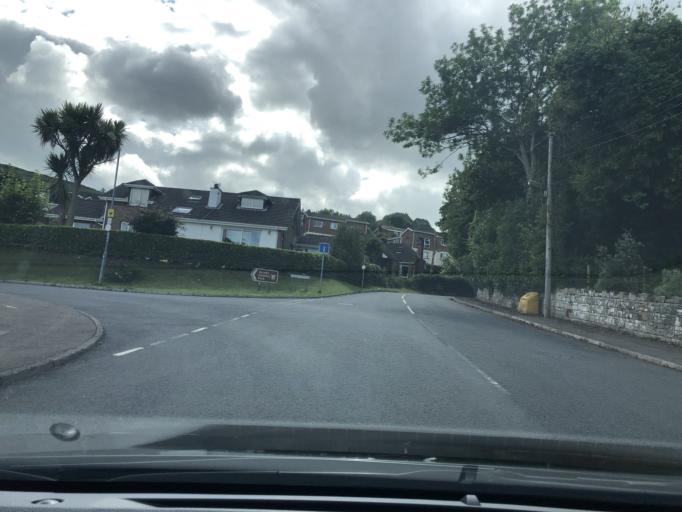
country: GB
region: Northern Ireland
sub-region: Ards District
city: Newtownards
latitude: 54.5881
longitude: -5.7140
